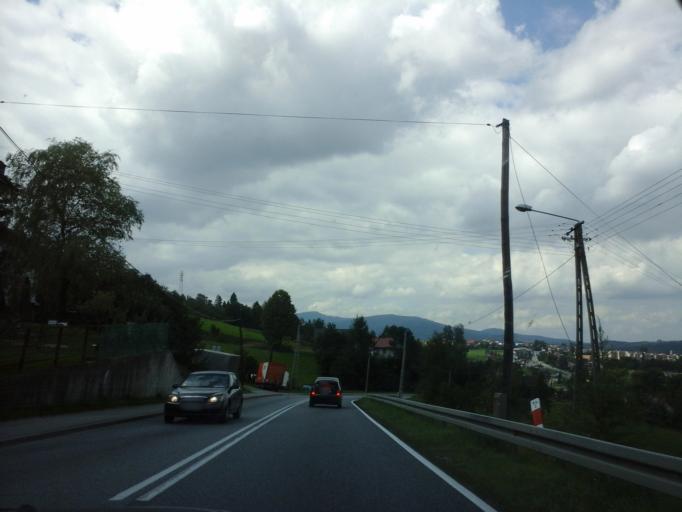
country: PL
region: Lesser Poland Voivodeship
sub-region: Powiat suski
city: Naprawa
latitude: 49.6456
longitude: 19.8547
